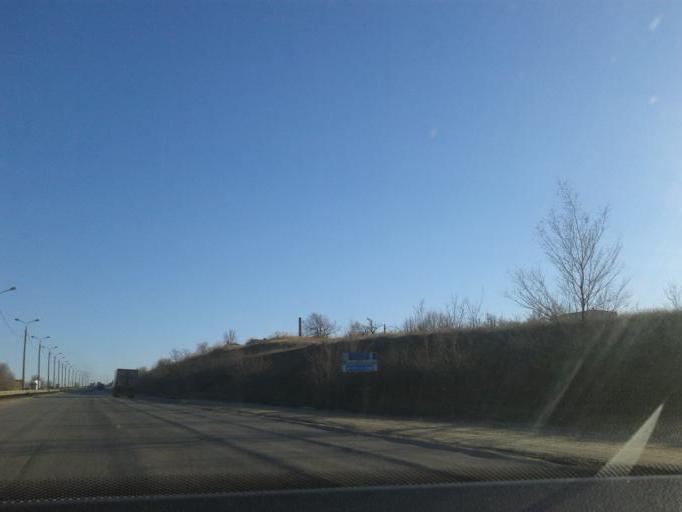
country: RU
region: Volgograd
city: Volgograd
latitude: 48.7110
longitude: 44.4425
